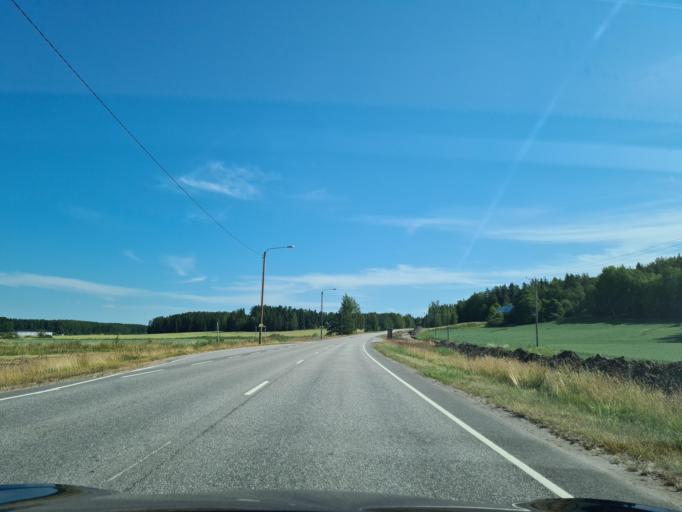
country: FI
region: Varsinais-Suomi
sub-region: Turku
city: Paimio
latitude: 60.4480
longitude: 22.6093
